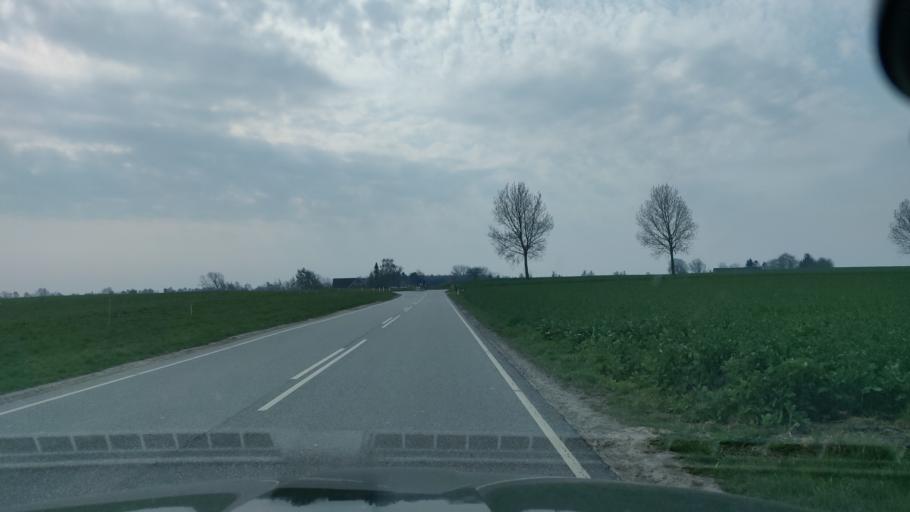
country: DK
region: South Denmark
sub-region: Nordfyns Kommune
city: Sonderso
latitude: 55.4984
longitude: 10.2488
